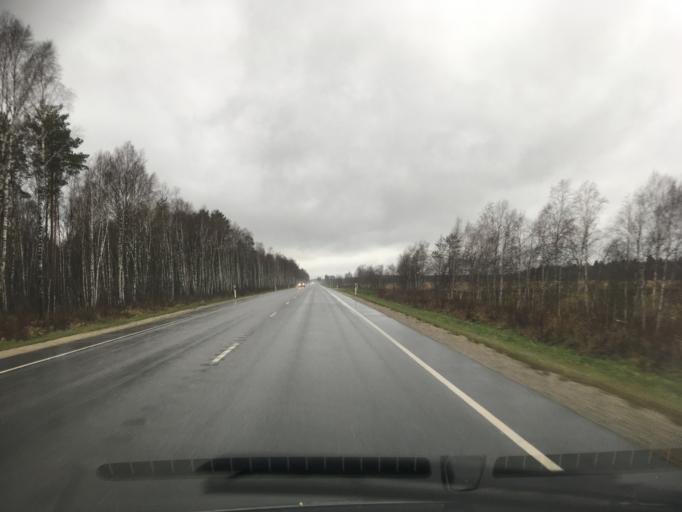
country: EE
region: Laeaene
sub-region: Lihula vald
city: Lihula
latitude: 58.7897
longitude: 24.0280
